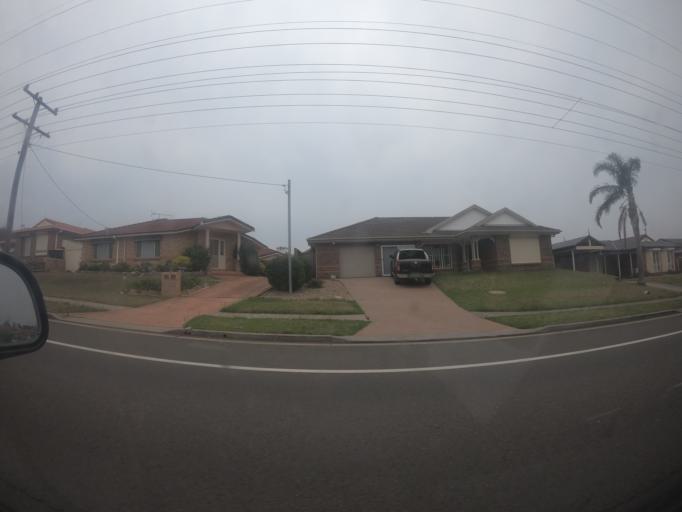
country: AU
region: New South Wales
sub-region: Shellharbour
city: Barrack Heights
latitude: -34.5745
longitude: 150.8391
